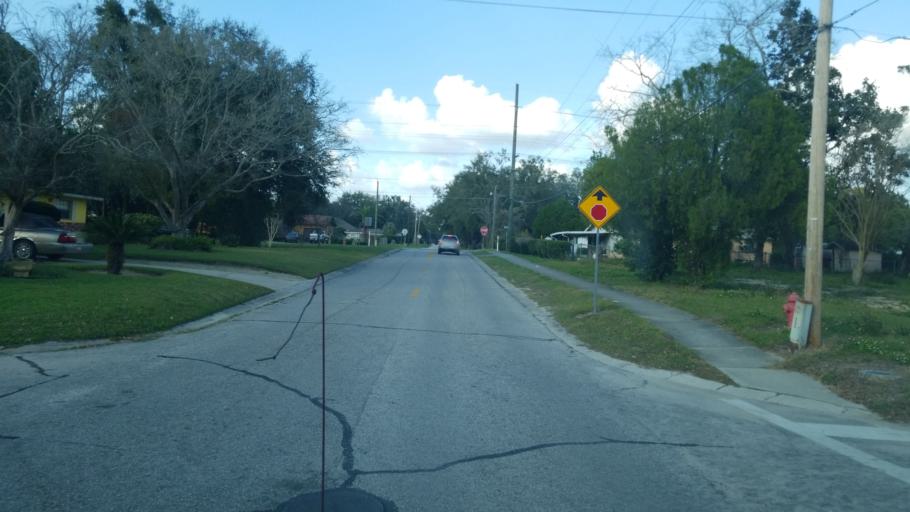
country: US
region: Florida
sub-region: Marion County
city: Ocala
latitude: 29.1817
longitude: -82.1604
